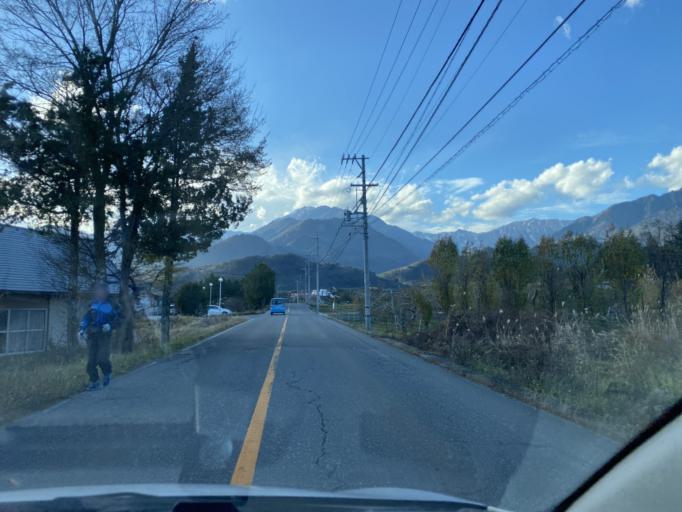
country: JP
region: Nagano
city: Omachi
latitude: 36.5276
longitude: 137.8203
